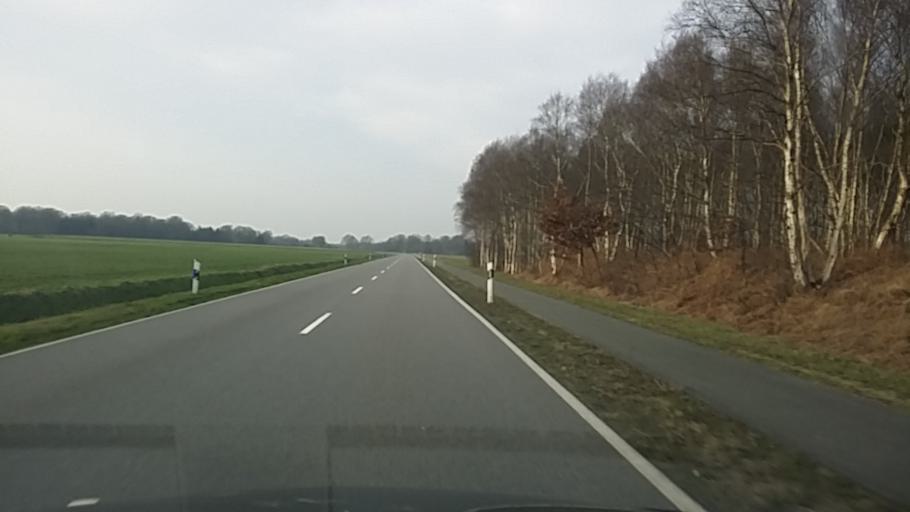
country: DE
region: Lower Saxony
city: Georgsdorf
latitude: 52.6041
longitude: 7.1258
